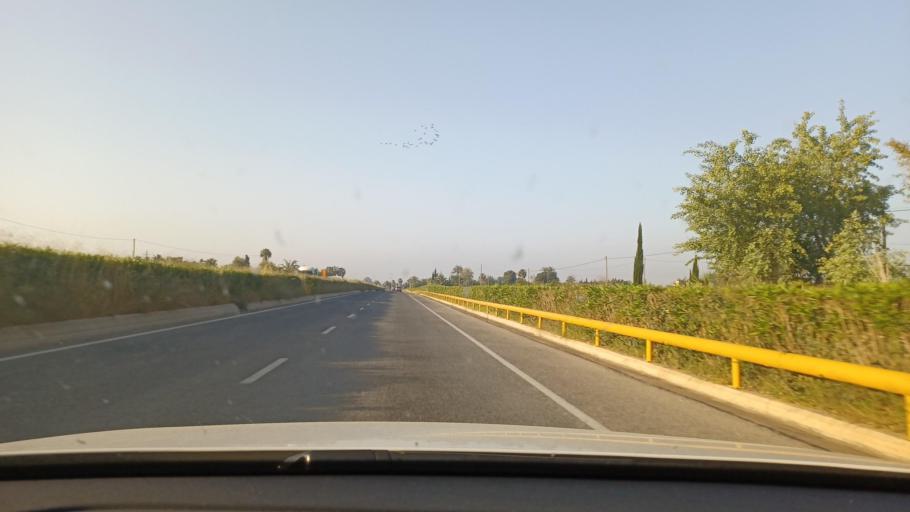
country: ES
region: Valencia
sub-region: Provincia de Alicante
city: Elche
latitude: 38.1846
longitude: -0.7015
